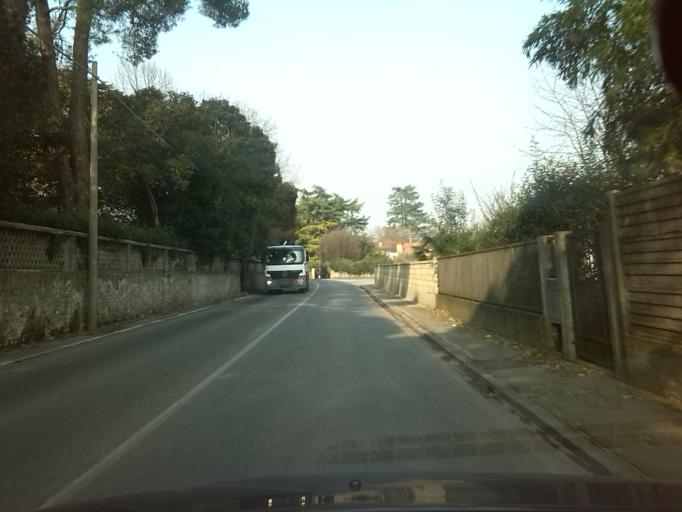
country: IT
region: Friuli Venezia Giulia
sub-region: Provincia di Gorizia
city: Gradisca d'Isonzo
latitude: 45.8948
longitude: 13.4997
